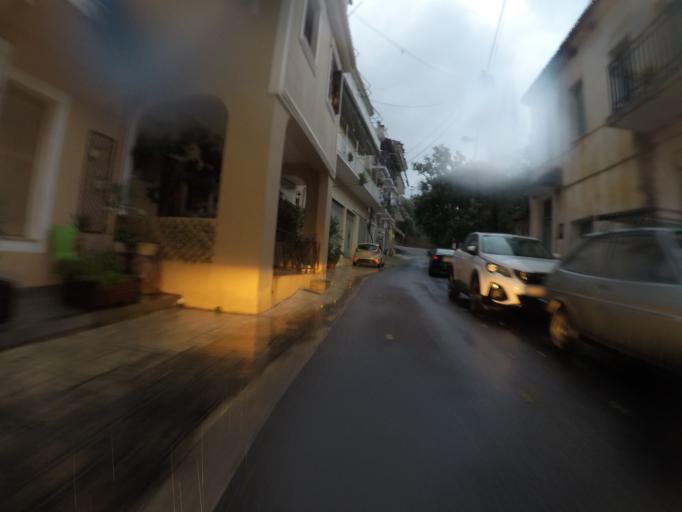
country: GR
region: Peloponnese
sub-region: Nomos Messinias
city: Pylos
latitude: 36.9123
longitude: 21.6966
